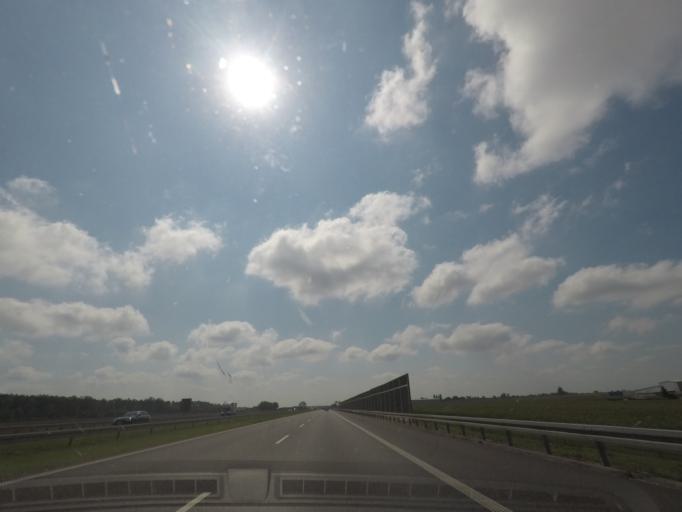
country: PL
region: Kujawsko-Pomorskie
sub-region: Powiat wloclawski
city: Brzesc Kujawski
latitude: 52.6378
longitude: 18.9508
